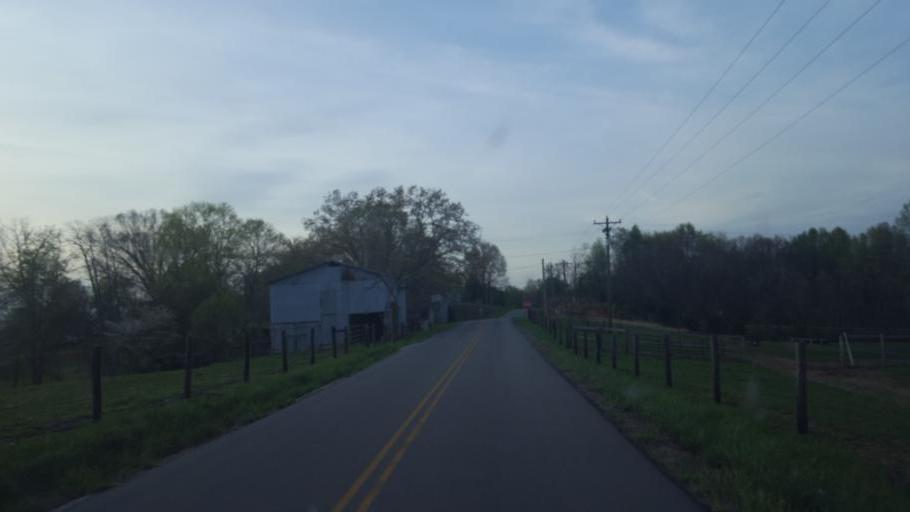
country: US
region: Kentucky
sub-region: Metcalfe County
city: Edmonton
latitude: 37.0764
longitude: -85.7070
